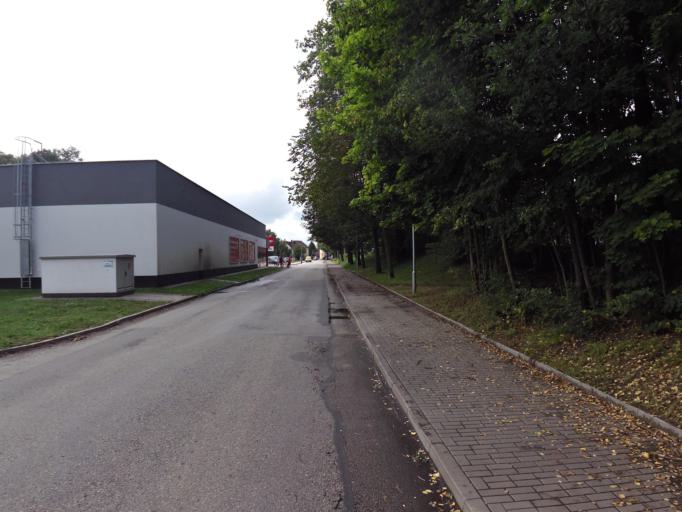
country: CZ
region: Jihocesky
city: Suchdol nad Luznici
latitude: 48.8933
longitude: 14.8805
